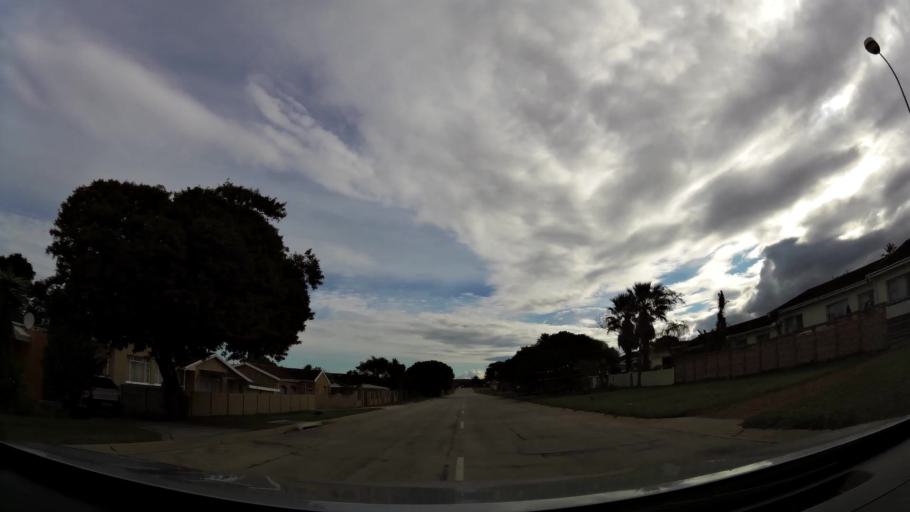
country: ZA
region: Eastern Cape
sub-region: Nelson Mandela Bay Metropolitan Municipality
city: Port Elizabeth
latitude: -33.9423
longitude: 25.4760
